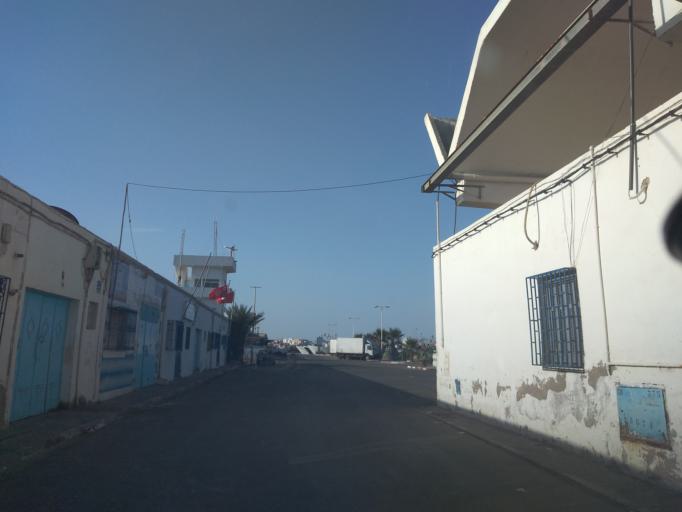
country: TN
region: Safaqis
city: Sfax
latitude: 34.7141
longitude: 10.7647
